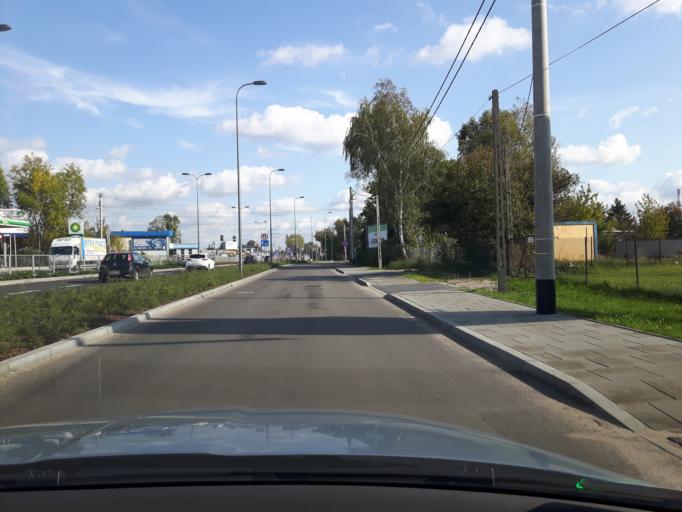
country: PL
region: Masovian Voivodeship
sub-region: Powiat wolominski
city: Zabki
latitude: 52.2862
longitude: 21.0904
